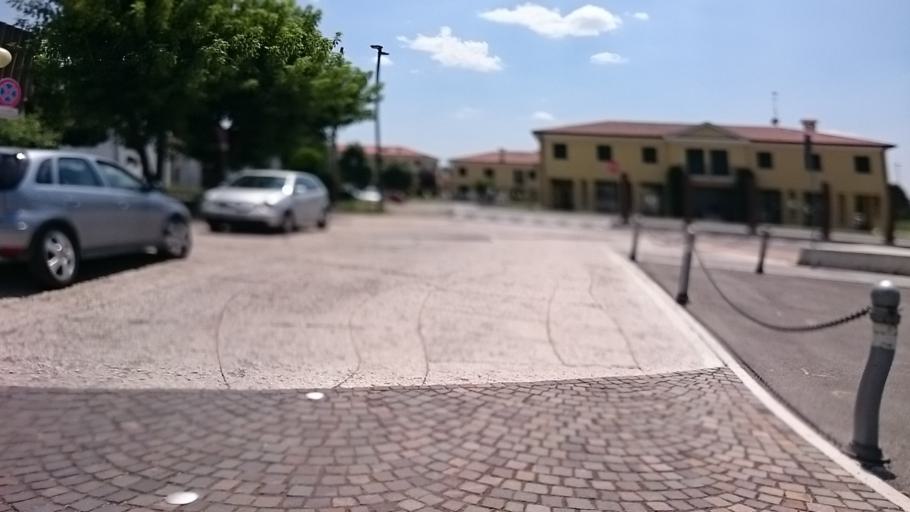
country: IT
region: Veneto
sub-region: Provincia di Padova
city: Villanova
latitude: 45.4902
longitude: 11.9724
